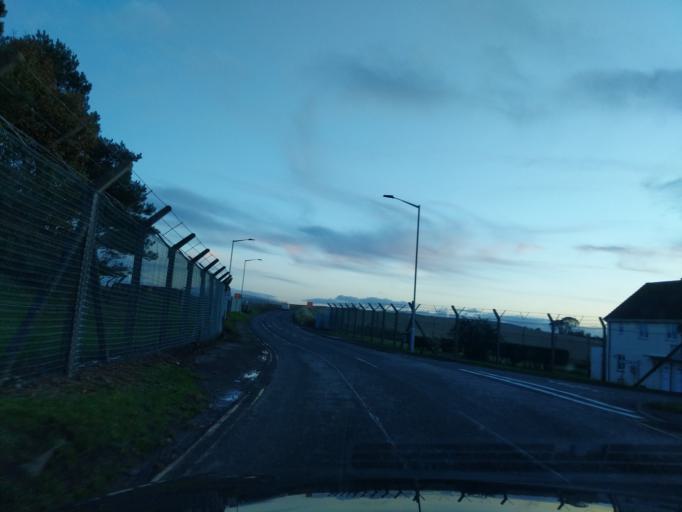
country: GB
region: Scotland
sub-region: Fife
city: Leuchars
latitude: 56.3753
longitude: -2.8866
